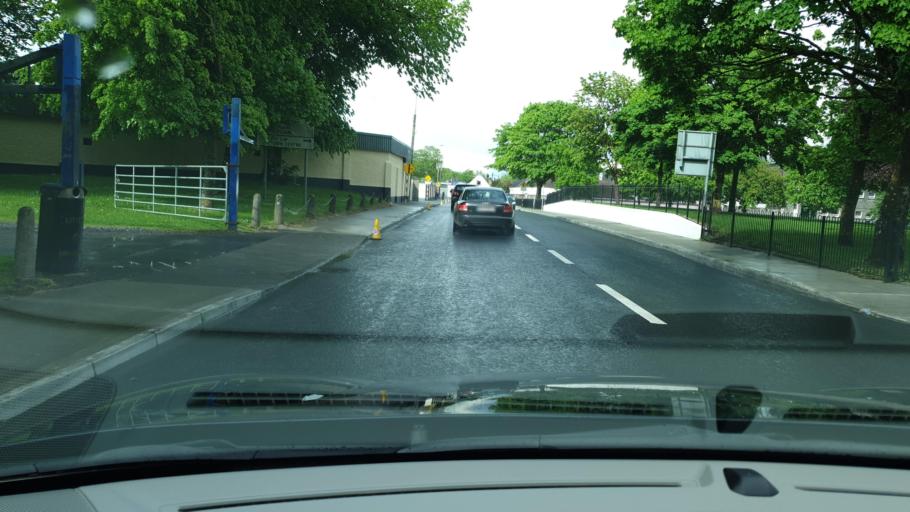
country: IE
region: Connaught
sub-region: County Galway
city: Ballinasloe
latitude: 53.3296
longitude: -8.2286
